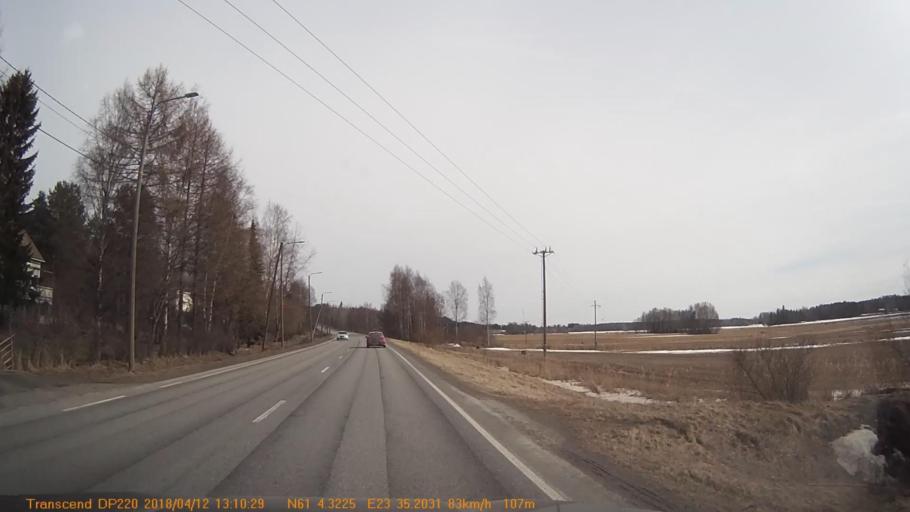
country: FI
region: Pirkanmaa
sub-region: Etelae-Pirkanmaa
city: Urjala
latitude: 61.0719
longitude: 23.5885
